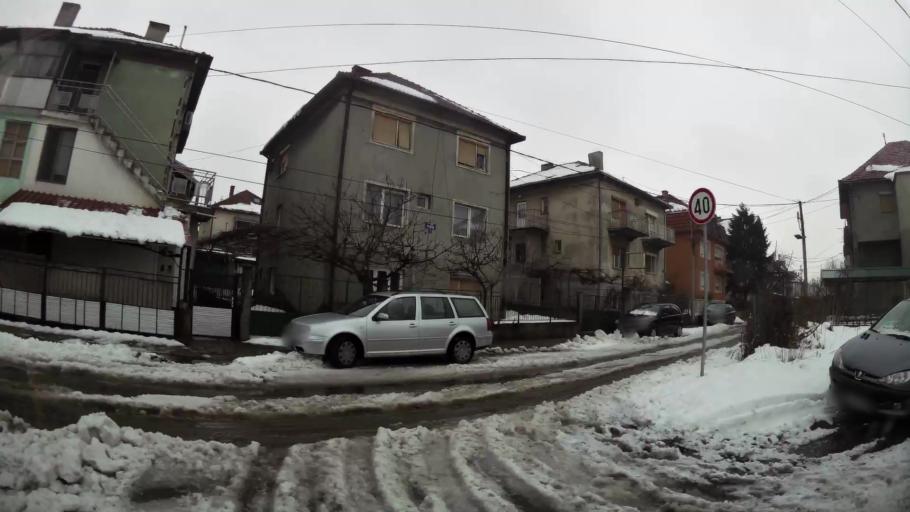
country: RS
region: Central Serbia
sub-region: Belgrade
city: Zemun
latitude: 44.8417
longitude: 20.3713
